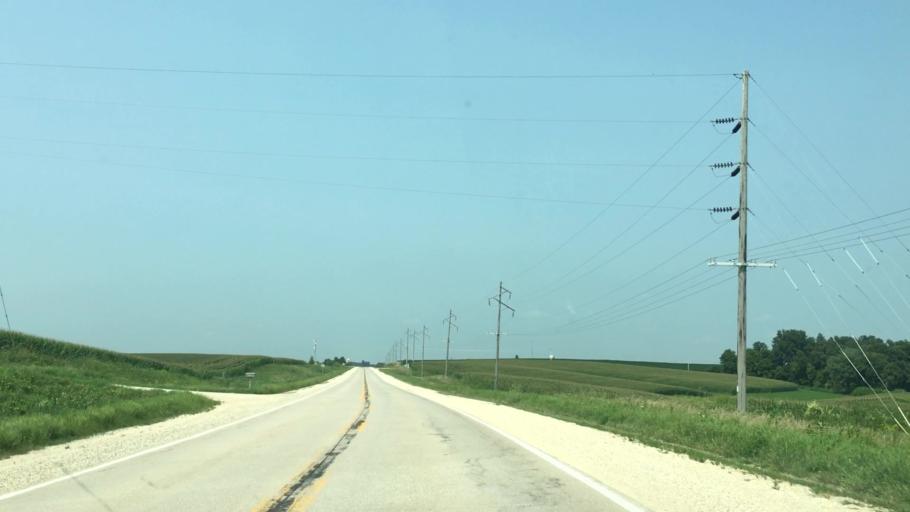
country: US
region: Iowa
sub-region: Winneshiek County
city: Decorah
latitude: 43.1434
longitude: -91.8642
